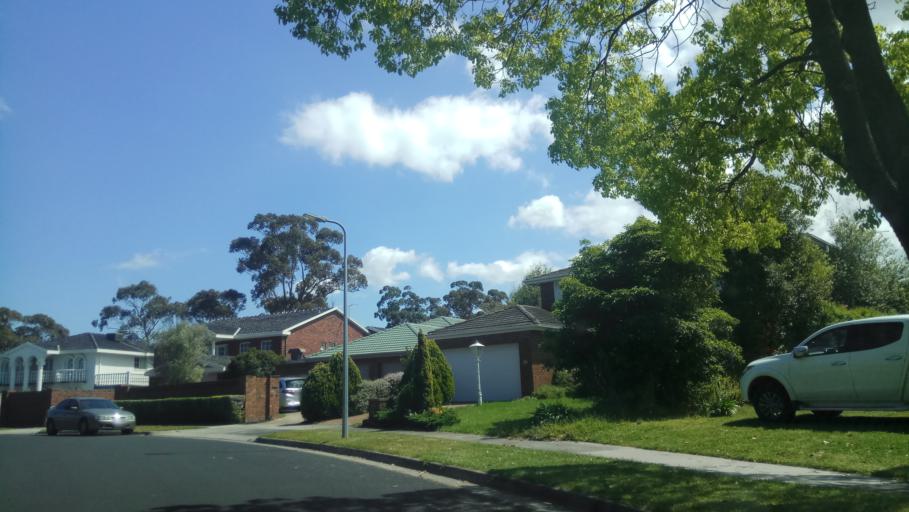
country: AU
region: Victoria
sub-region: Kingston
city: Dingley Village
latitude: -37.9767
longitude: 145.1294
